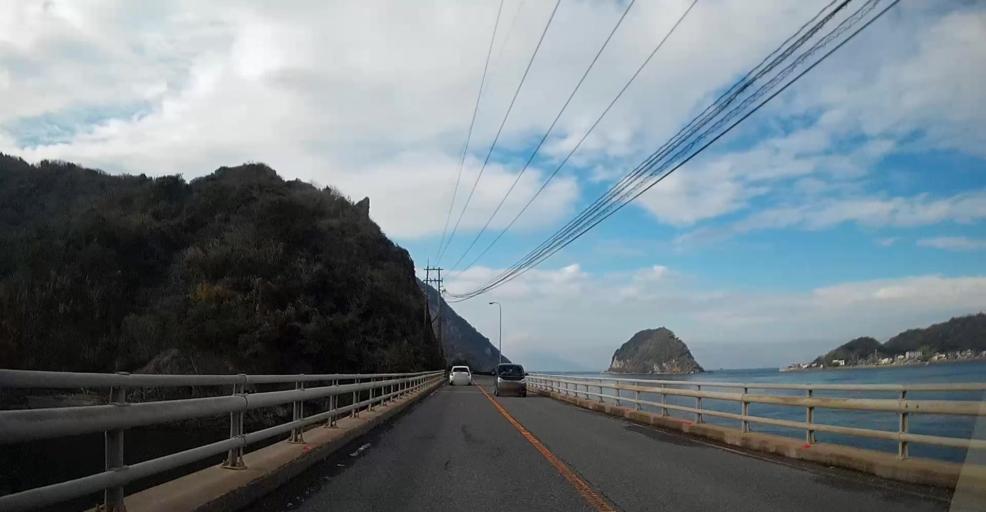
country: JP
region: Kumamoto
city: Yatsushiro
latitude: 32.6165
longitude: 130.4517
